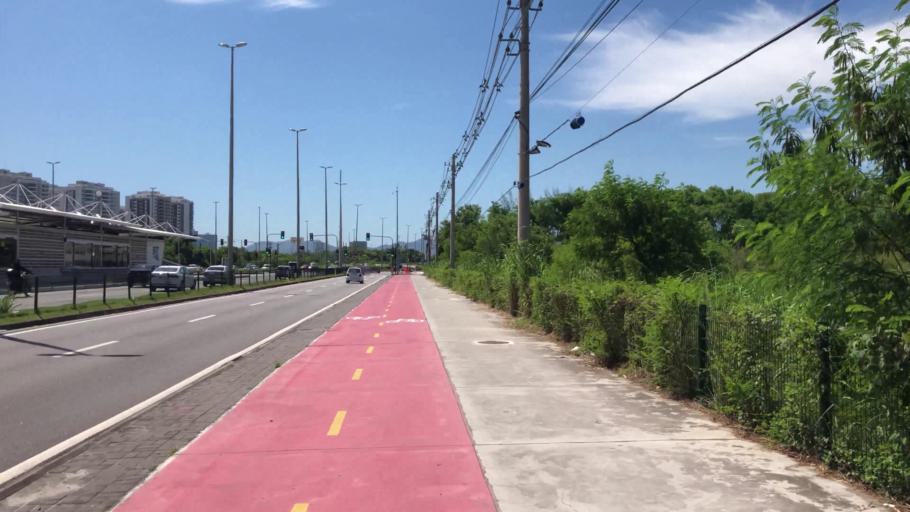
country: BR
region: Rio de Janeiro
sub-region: Nilopolis
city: Nilopolis
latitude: -22.9735
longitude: -43.3950
